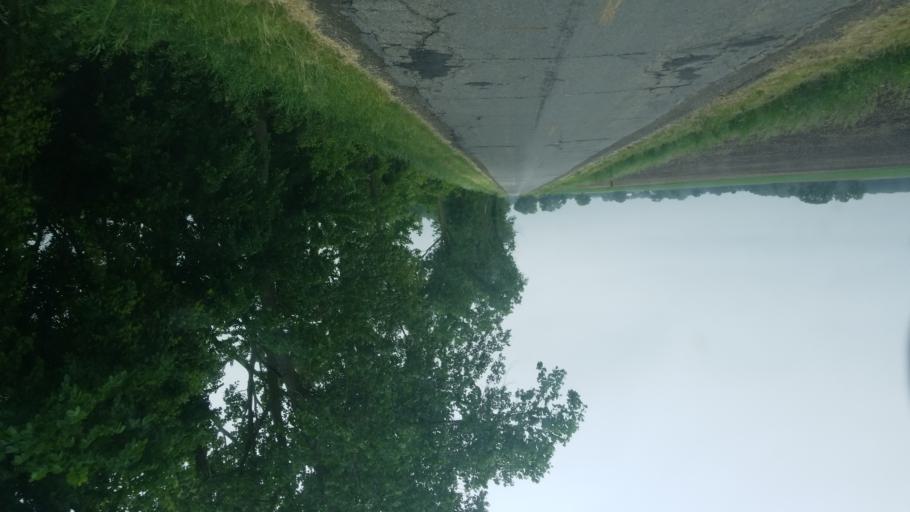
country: US
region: Indiana
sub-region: Marshall County
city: Bremen
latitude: 41.5013
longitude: -86.1179
